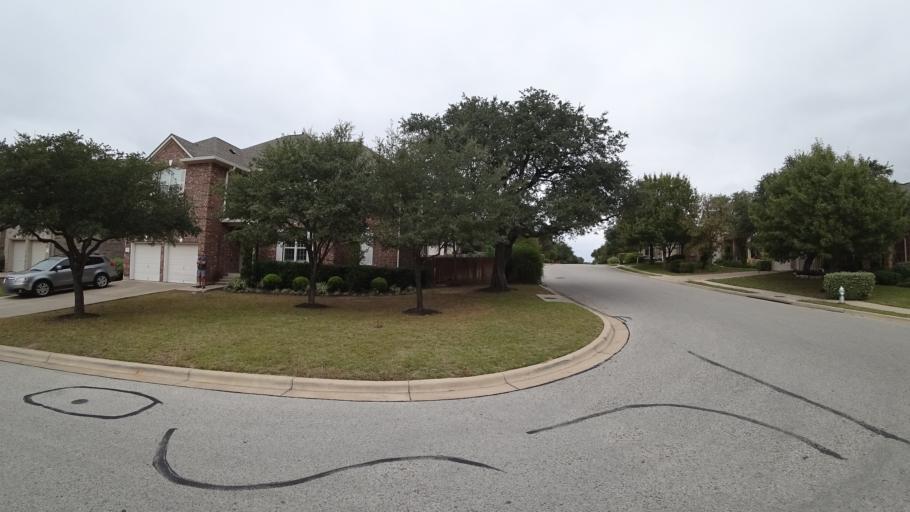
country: US
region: Texas
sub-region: Travis County
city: Bee Cave
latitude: 30.3524
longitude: -97.9049
